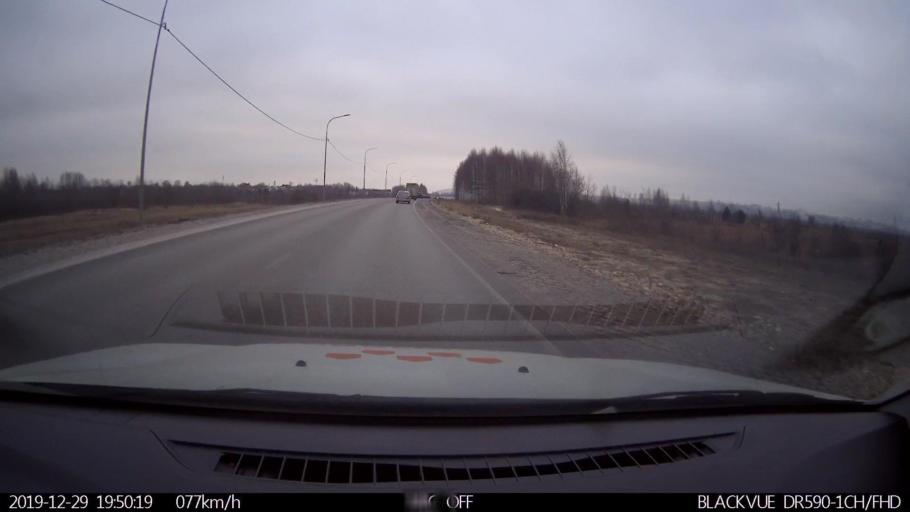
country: RU
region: Nizjnij Novgorod
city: Nizhniy Novgorod
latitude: 56.3693
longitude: 44.0268
